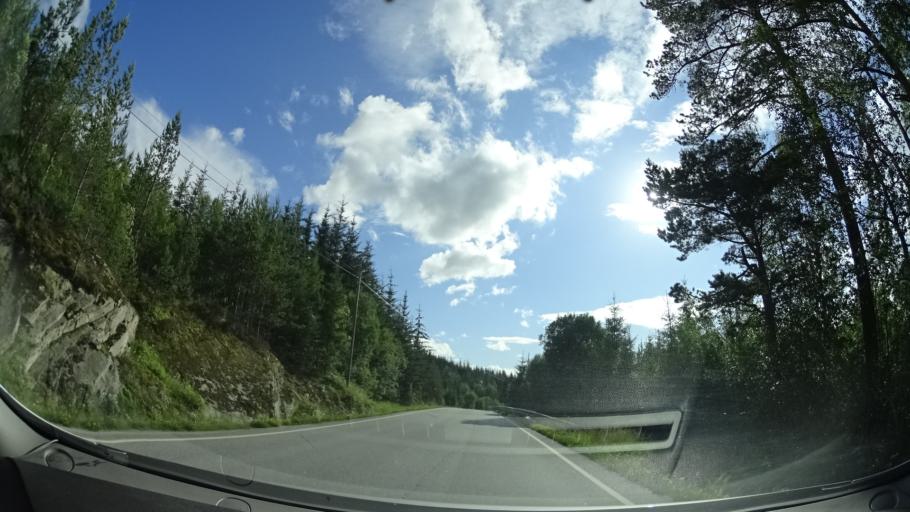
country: NO
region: More og Romsdal
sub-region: Halsa
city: Liaboen
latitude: 63.0745
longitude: 8.3074
